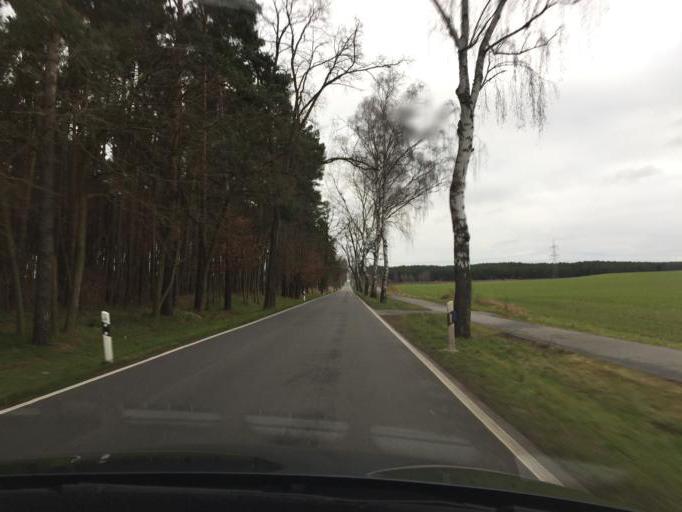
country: DE
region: Brandenburg
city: Gross Lindow
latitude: 52.1149
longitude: 14.5050
